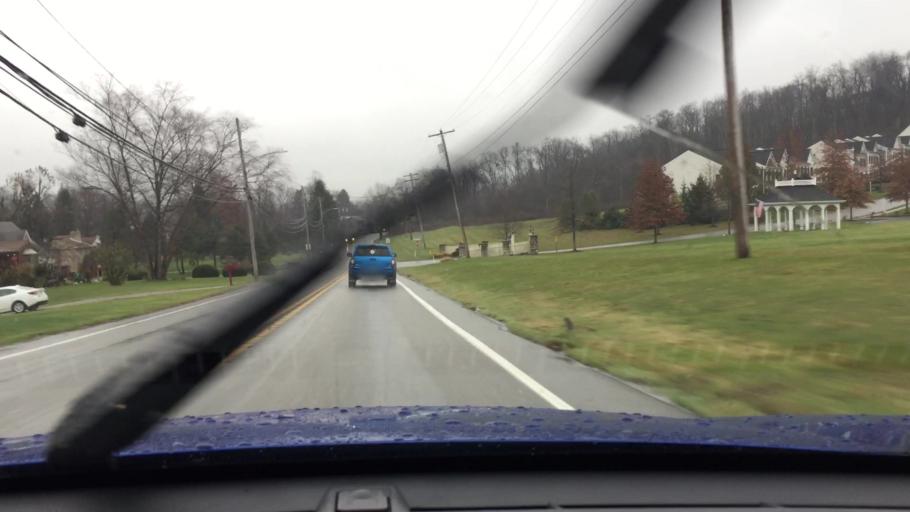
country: US
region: Pennsylvania
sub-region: Washington County
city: Canonsburg
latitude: 40.2741
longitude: -80.1514
